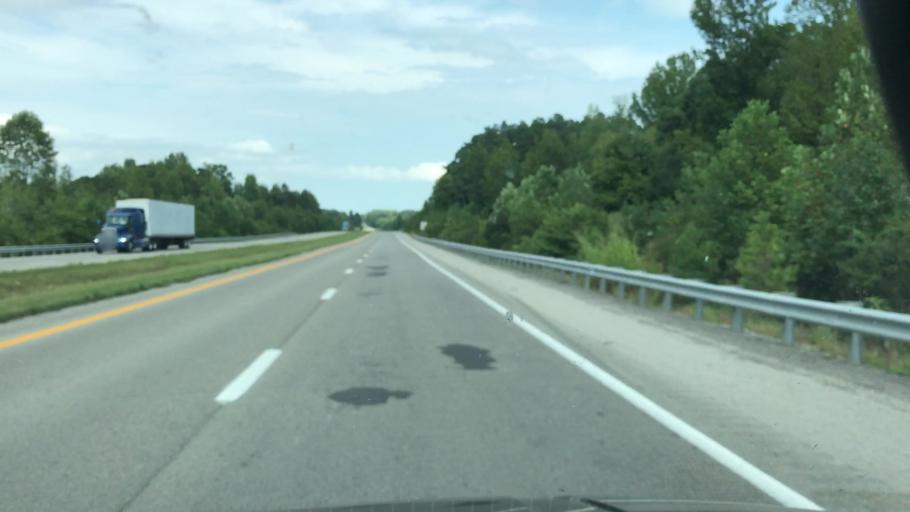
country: US
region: Kentucky
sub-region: Hopkins County
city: Earlington
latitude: 37.2016
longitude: -87.5302
